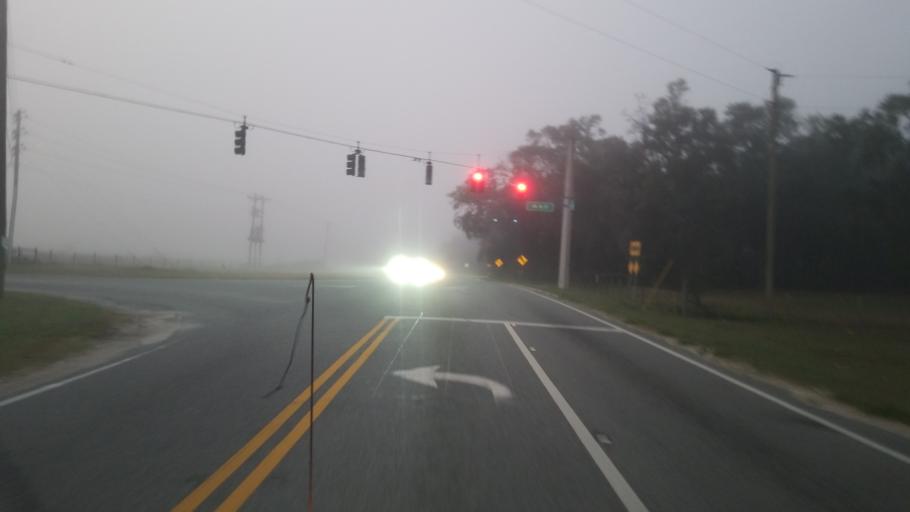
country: US
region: Florida
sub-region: Marion County
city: Ocala
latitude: 29.1505
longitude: -82.2519
